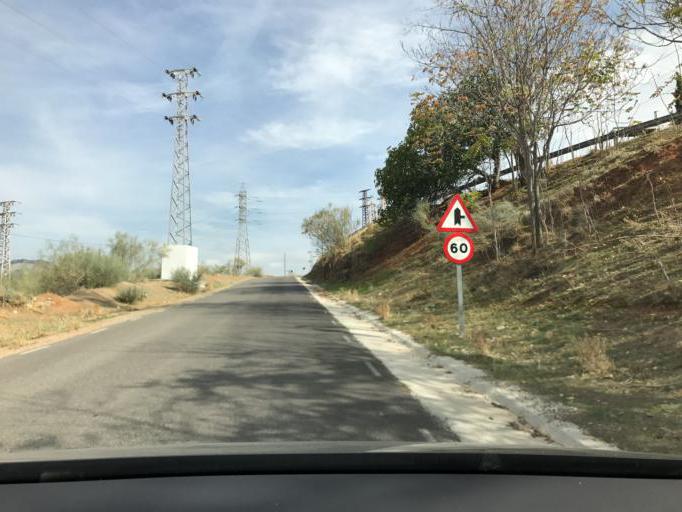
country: ES
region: Andalusia
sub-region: Provincia de Granada
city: Jun
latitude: 37.1965
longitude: -3.5779
